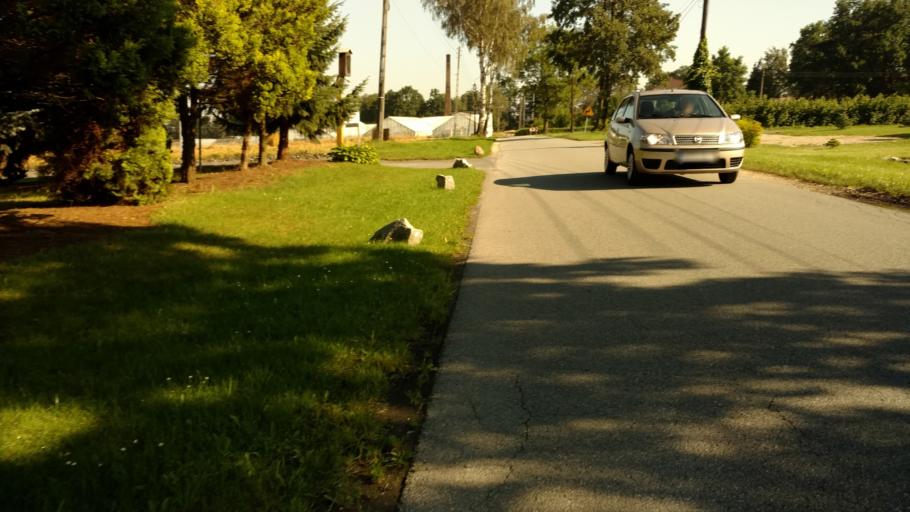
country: PL
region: Silesian Voivodeship
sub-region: Powiat pszczynski
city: Jankowice
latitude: 49.9805
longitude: 18.9830
